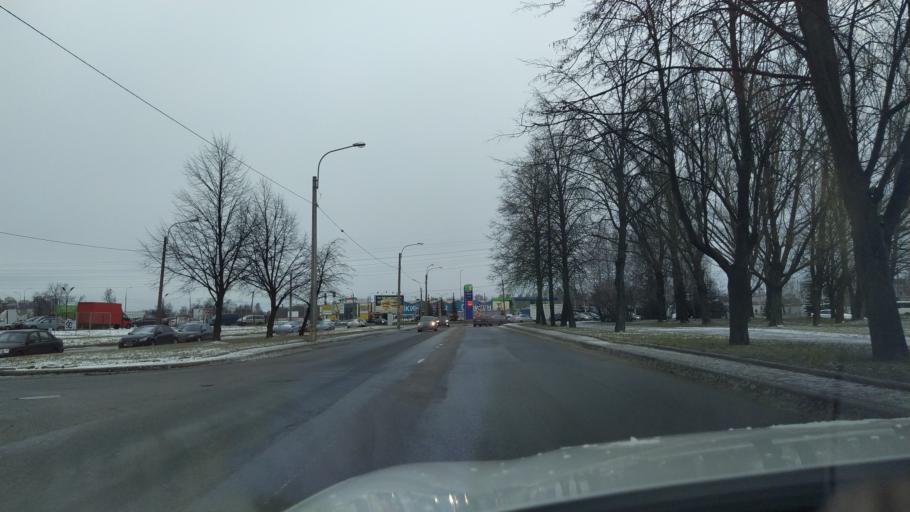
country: RU
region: St.-Petersburg
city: Grazhdanka
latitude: 60.0136
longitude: 30.4312
